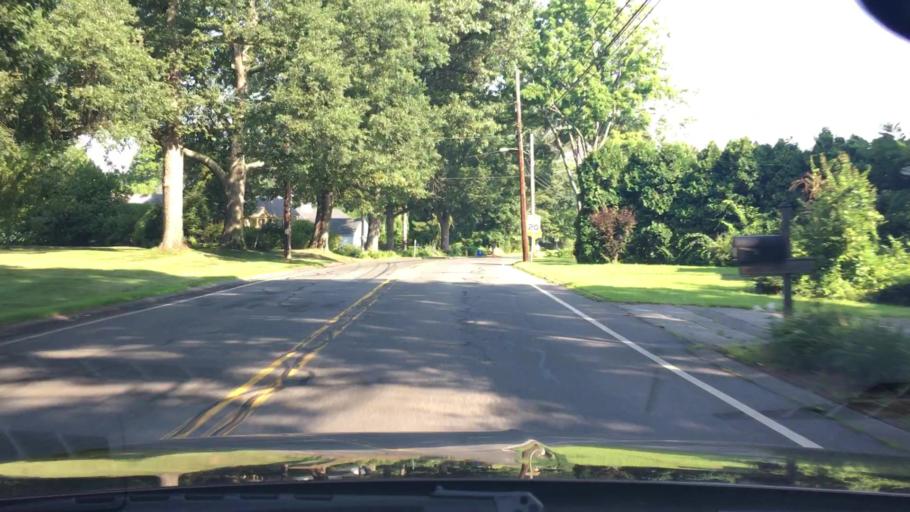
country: US
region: Massachusetts
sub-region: Hampden County
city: East Longmeadow
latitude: 42.0525
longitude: -72.5104
